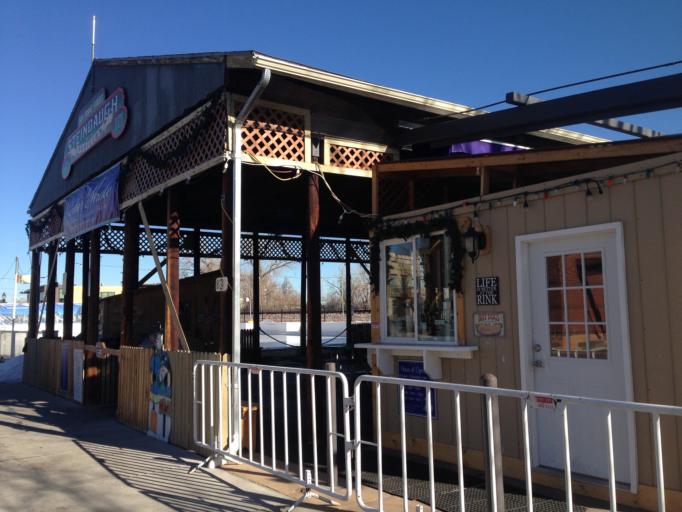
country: US
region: Colorado
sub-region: Boulder County
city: Louisville
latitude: 39.9783
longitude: -105.1307
